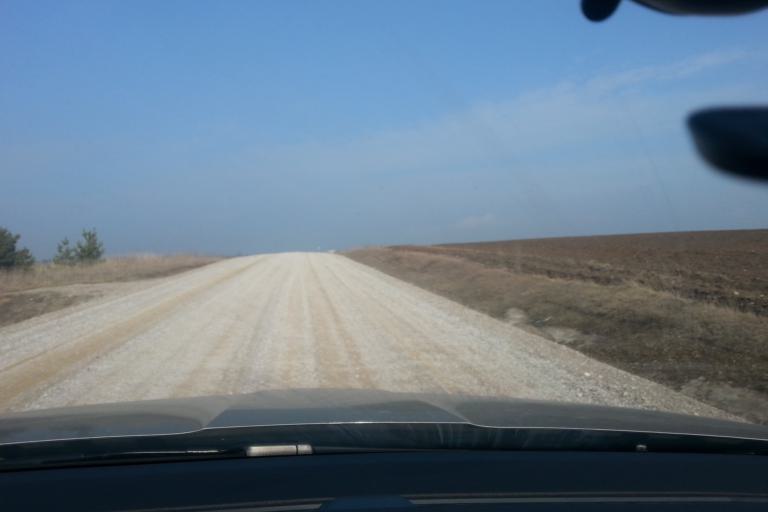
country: LT
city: Trakai
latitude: 54.5909
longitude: 24.9773
